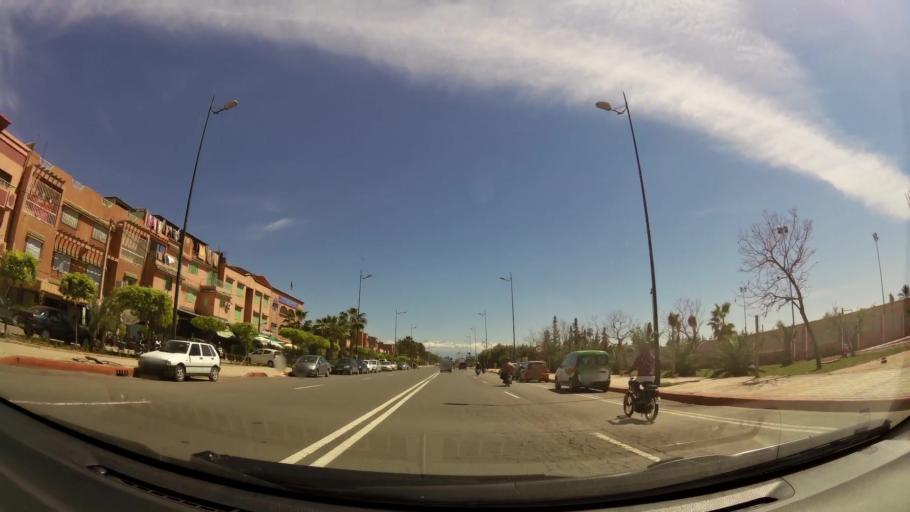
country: MA
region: Marrakech-Tensift-Al Haouz
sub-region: Marrakech
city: Marrakesh
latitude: 31.6060
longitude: -7.9727
